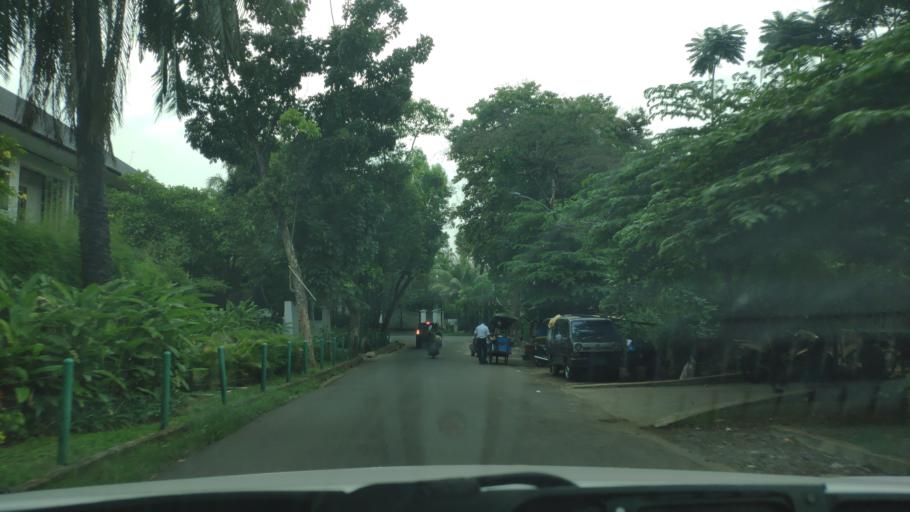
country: ID
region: Jakarta Raya
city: Jakarta
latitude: -6.2349
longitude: 106.8049
